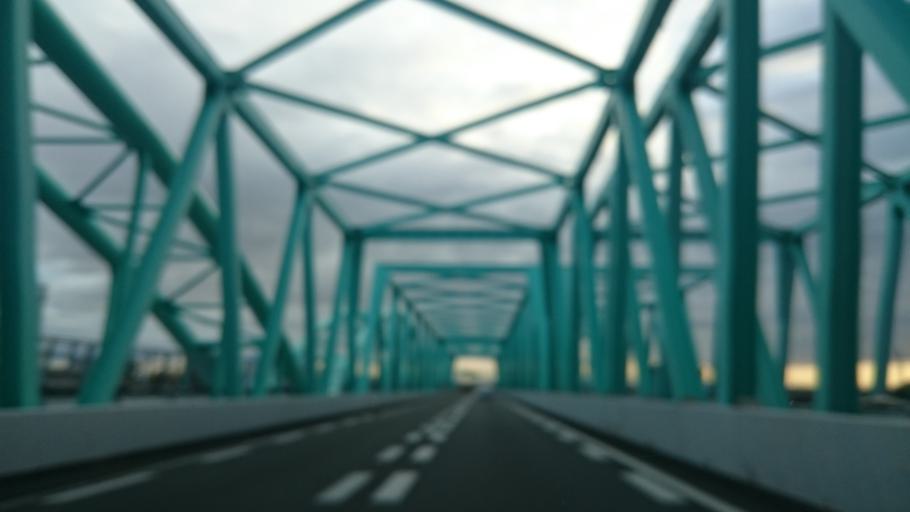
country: JP
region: Aichi
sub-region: Tsushima-shi
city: Tsushima
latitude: 35.1175
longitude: 136.7066
